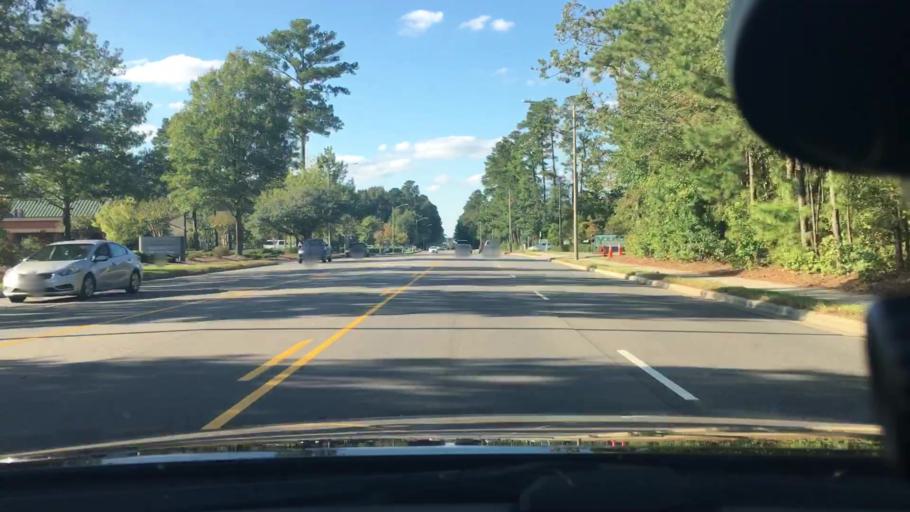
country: US
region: North Carolina
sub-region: Pitt County
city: Windsor
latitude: 35.5749
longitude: -77.3612
